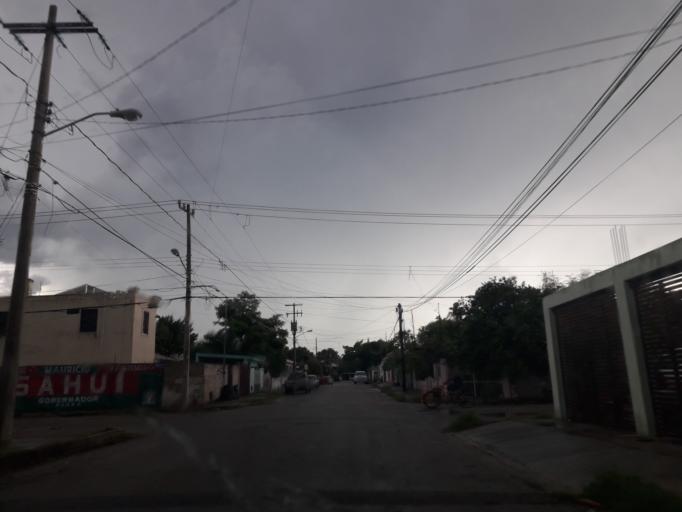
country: MX
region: Yucatan
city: Merida
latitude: 20.9794
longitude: -89.6531
